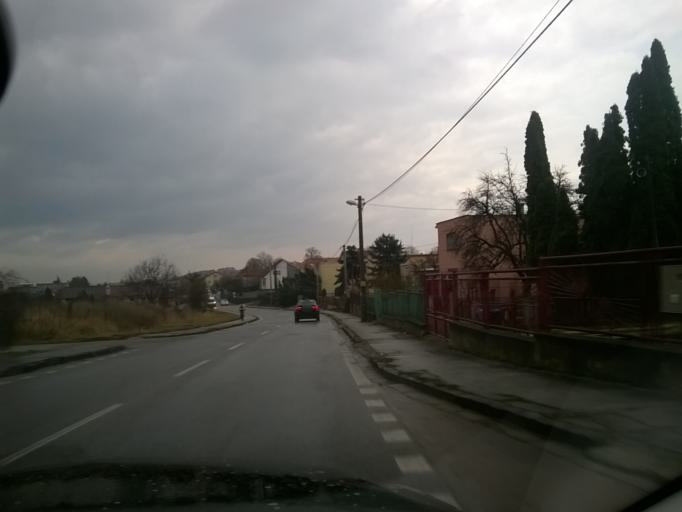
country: SK
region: Nitriansky
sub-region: Okres Nitra
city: Nitra
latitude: 48.2960
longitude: 18.0695
